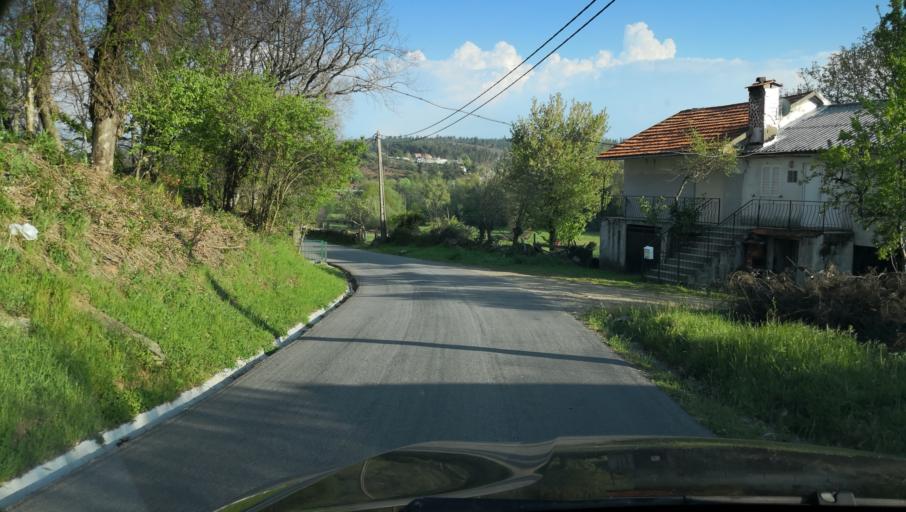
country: PT
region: Vila Real
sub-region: Santa Marta de Penaguiao
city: Santa Marta de Penaguiao
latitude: 41.2879
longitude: -7.8347
